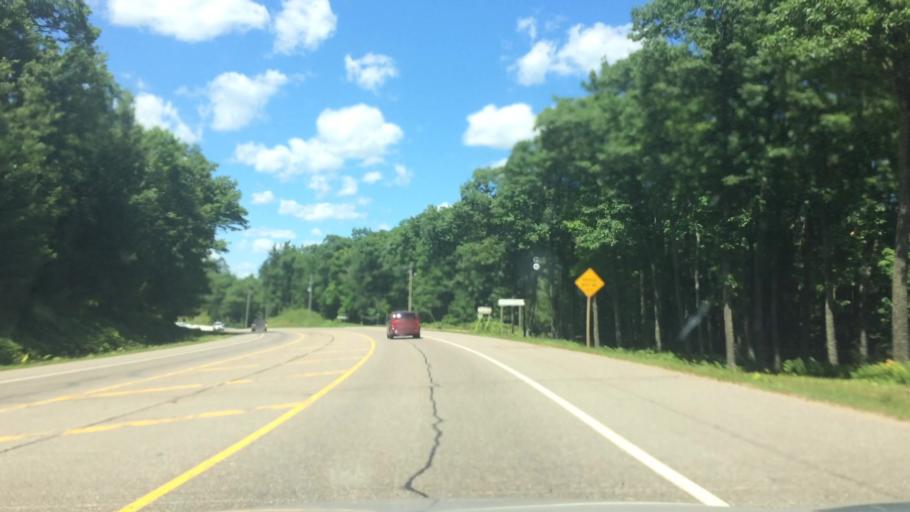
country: US
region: Wisconsin
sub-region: Vilas County
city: Lac du Flambeau
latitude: 45.7891
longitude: -89.7102
